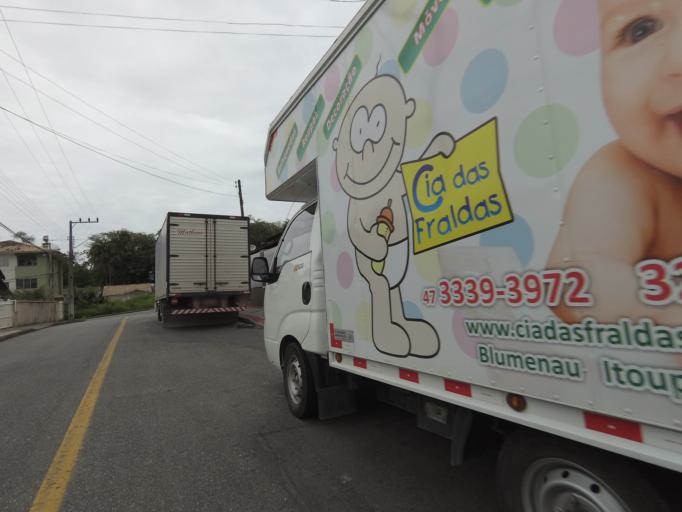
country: BR
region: Santa Catarina
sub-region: Blumenau
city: Blumenau
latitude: -26.9010
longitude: -49.1306
